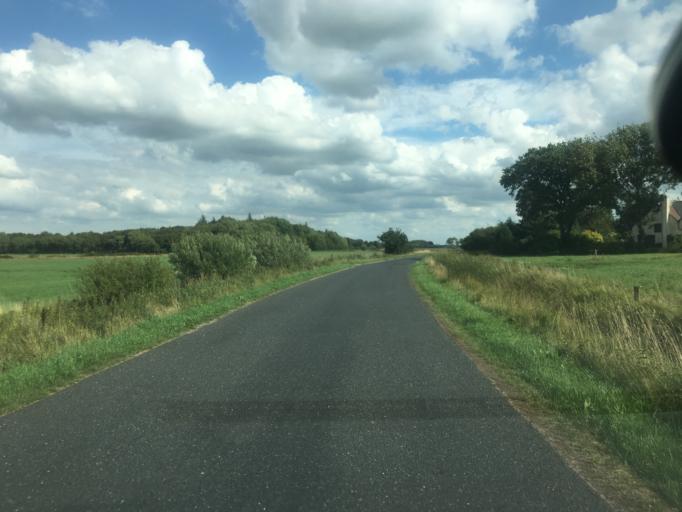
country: DK
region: South Denmark
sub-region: Tonder Kommune
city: Logumkloster
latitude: 55.0210
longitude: 8.9877
